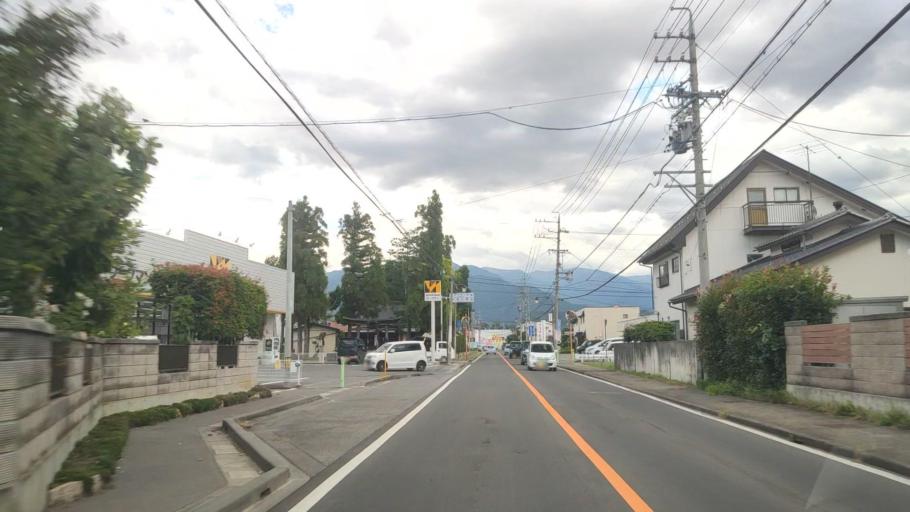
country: JP
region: Nagano
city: Suzaka
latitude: 36.6554
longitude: 138.2856
